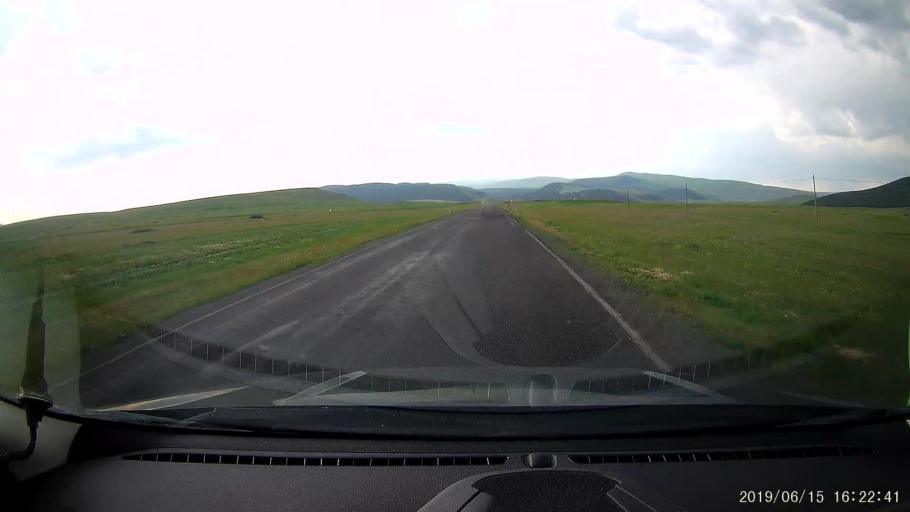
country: TR
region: Ardahan
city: Hanak
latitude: 41.1857
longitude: 42.8534
